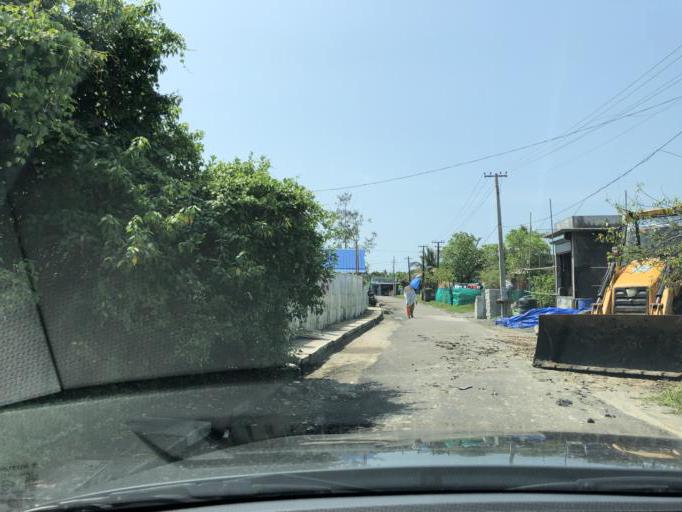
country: IN
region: Kerala
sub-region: Ernakulam
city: Cochin
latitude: 9.9936
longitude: 76.2349
